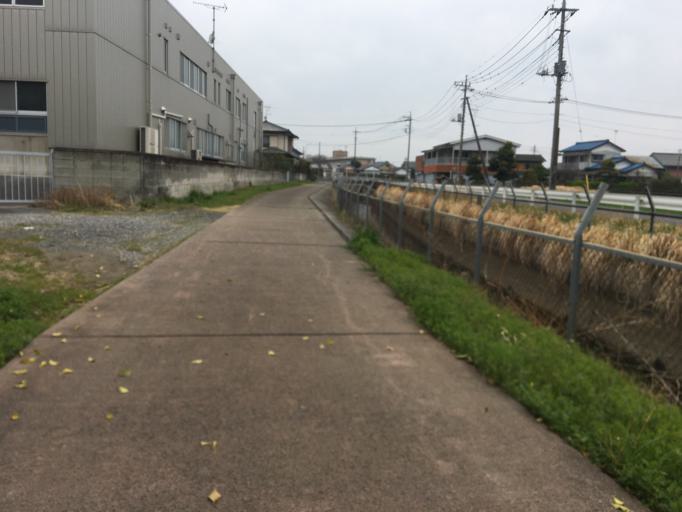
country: JP
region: Saitama
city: Kisai
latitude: 36.1131
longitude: 139.5868
